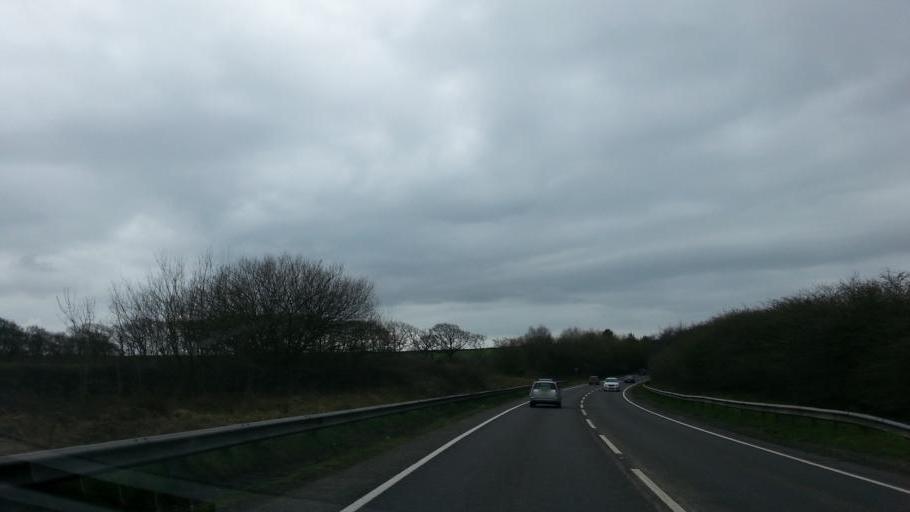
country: GB
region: England
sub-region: Devon
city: Fremington
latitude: 51.0450
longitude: -4.1276
